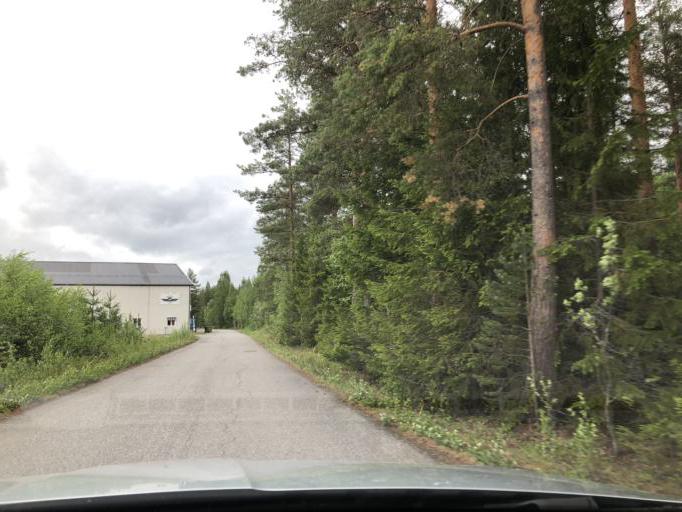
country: SE
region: Norrbotten
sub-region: Pitea Kommun
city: Roknas
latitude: 65.3907
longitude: 21.2697
